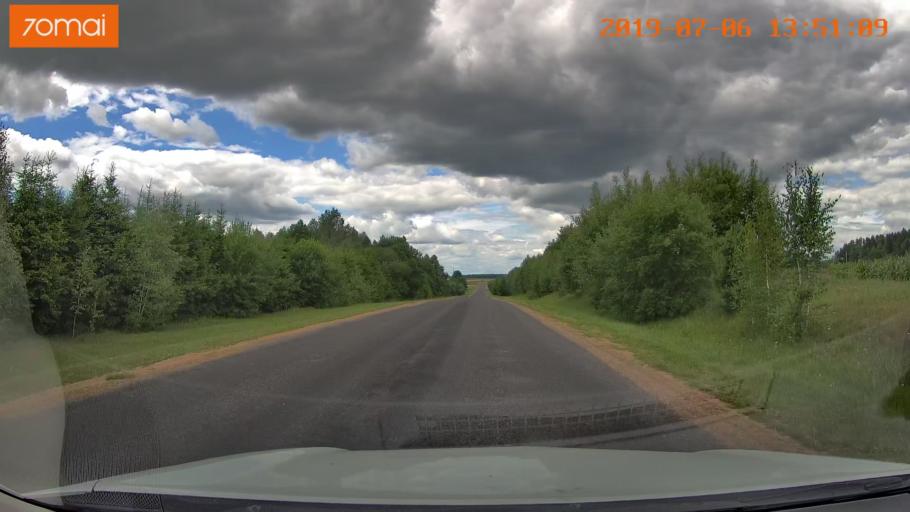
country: BY
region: Minsk
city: Ivyanyets
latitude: 53.7053
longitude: 26.8357
